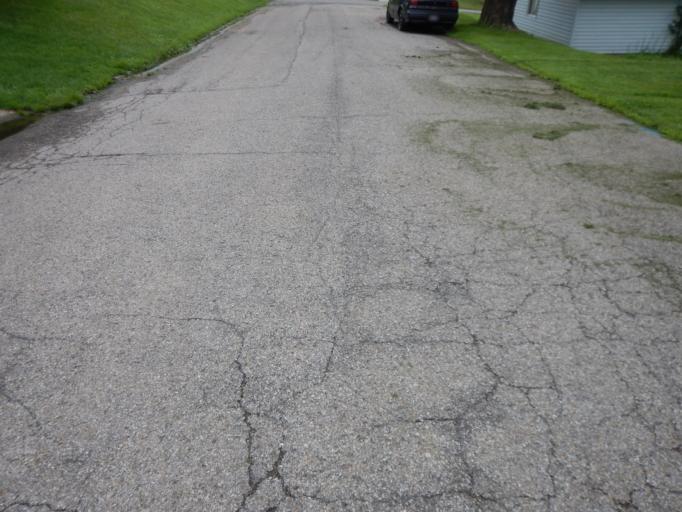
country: US
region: Ohio
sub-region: Muskingum County
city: North Zanesville
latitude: 39.9683
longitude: -82.0176
